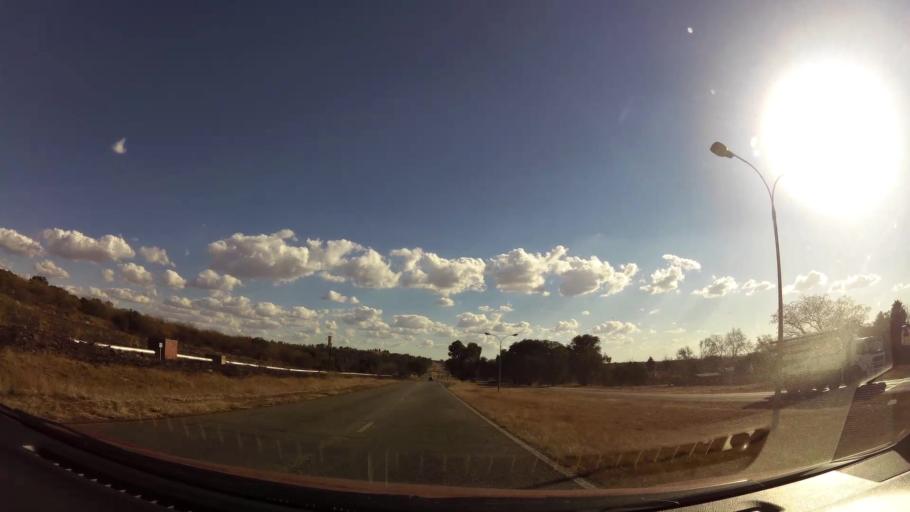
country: ZA
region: Gauteng
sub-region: West Rand District Municipality
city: Carletonville
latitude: -26.3756
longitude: 27.4011
